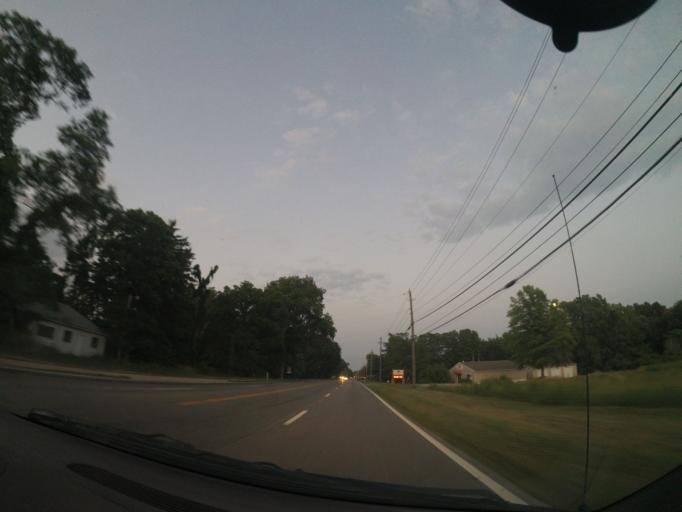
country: US
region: Ohio
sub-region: Lake County
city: North Madison
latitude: 41.8002
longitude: -81.0320
